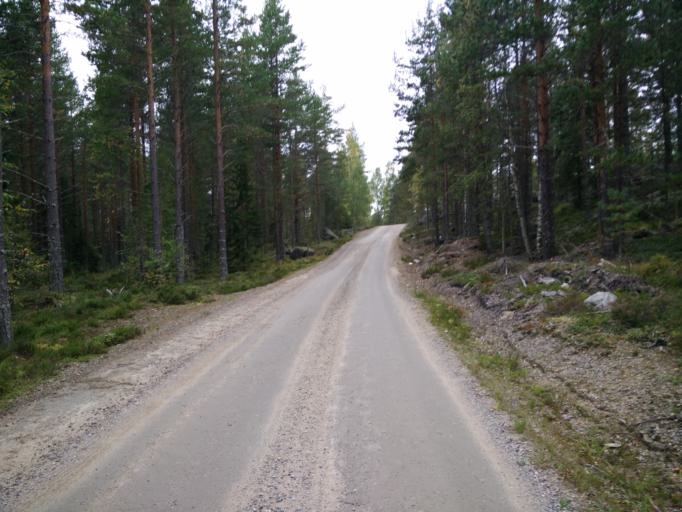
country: SE
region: Gaevleborg
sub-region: Hudiksvalls Kommun
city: Hudiksvall
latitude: 61.8339
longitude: 17.3252
